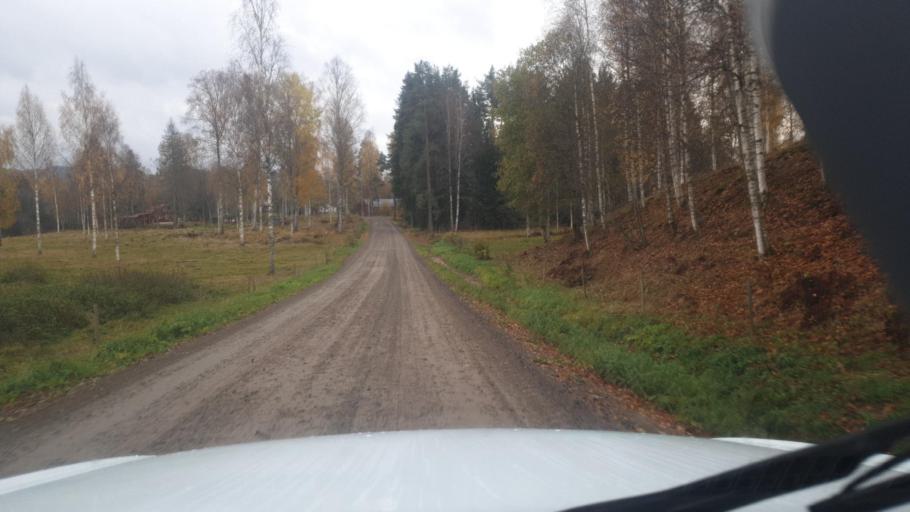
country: SE
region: Vaermland
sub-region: Torsby Kommun
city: Torsby
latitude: 59.9477
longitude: 12.9002
